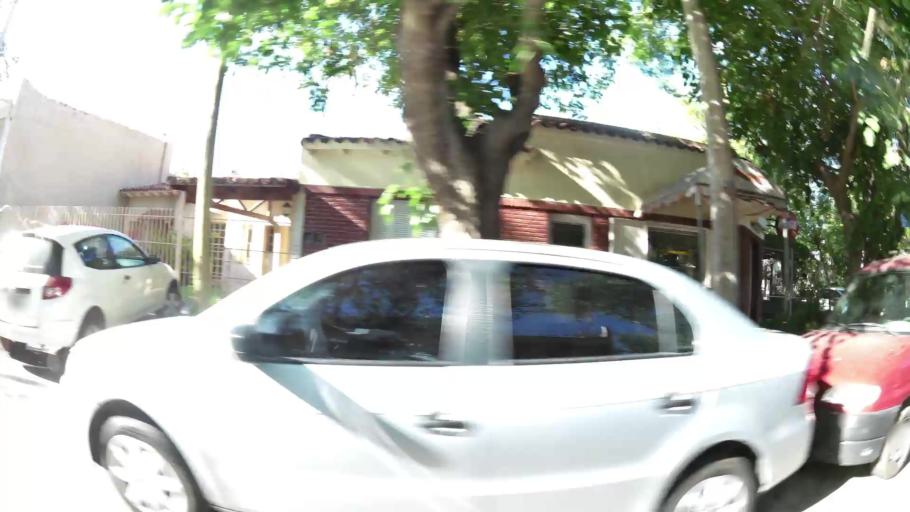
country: AR
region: Mendoza
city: Las Heras
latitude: -32.8689
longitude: -68.8512
